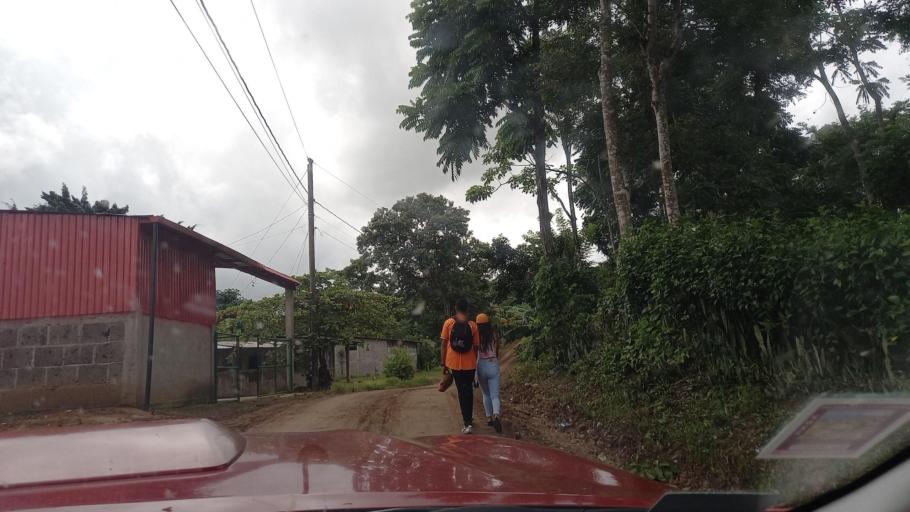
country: NI
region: Jinotega
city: San Jose de Bocay
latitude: 13.3480
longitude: -85.6574
